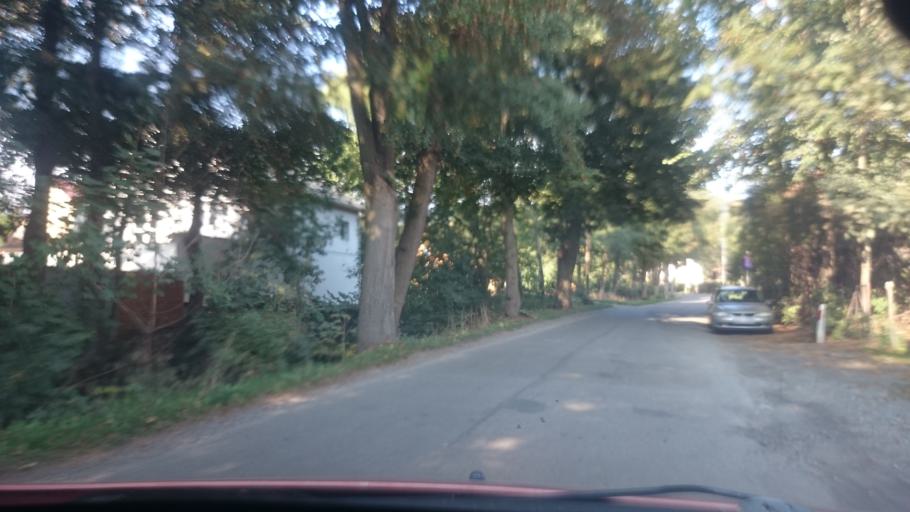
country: PL
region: Lower Silesian Voivodeship
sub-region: Powiat klodzki
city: Bystrzyca Klodzka
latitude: 50.3045
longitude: 16.6153
